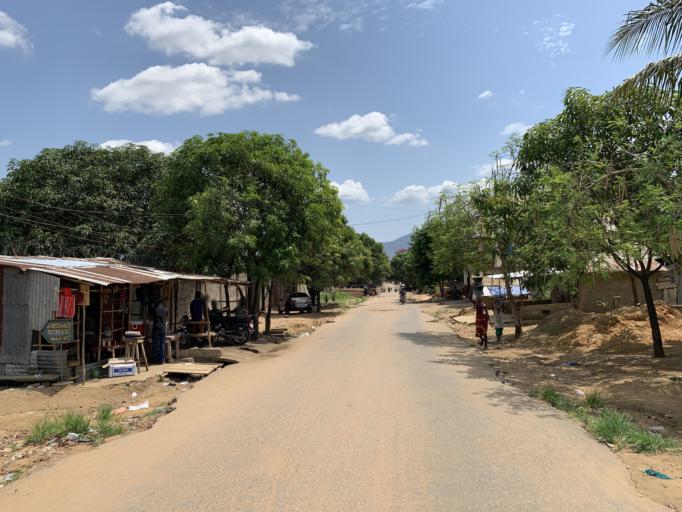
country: SL
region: Western Area
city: Waterloo
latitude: 8.3311
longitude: -13.0451
